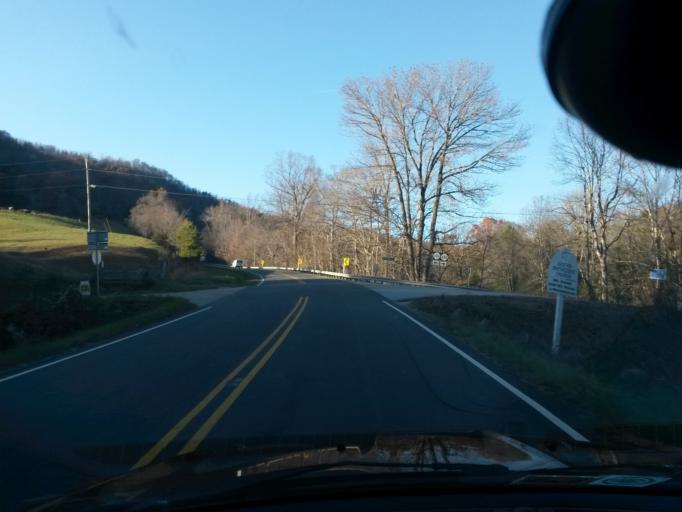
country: US
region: Virginia
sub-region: City of Buena Vista
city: Buena Vista
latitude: 37.6903
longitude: -79.2405
